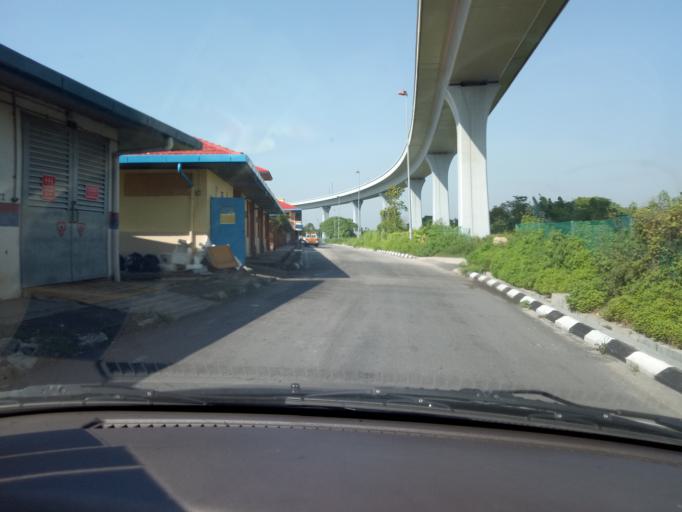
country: MY
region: Selangor
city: Kampong Baharu Balakong
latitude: 3.0343
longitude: 101.7701
